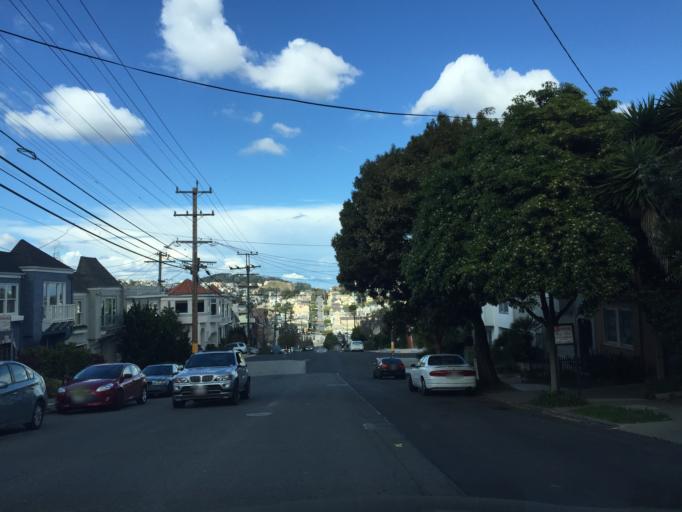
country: US
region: California
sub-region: San Francisco County
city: San Francisco
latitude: 37.7466
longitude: -122.4359
